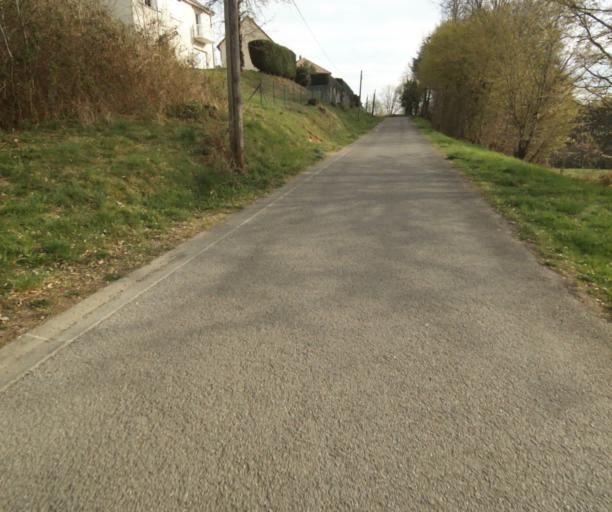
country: FR
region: Limousin
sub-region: Departement de la Correze
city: Naves
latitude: 45.3198
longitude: 1.7562
